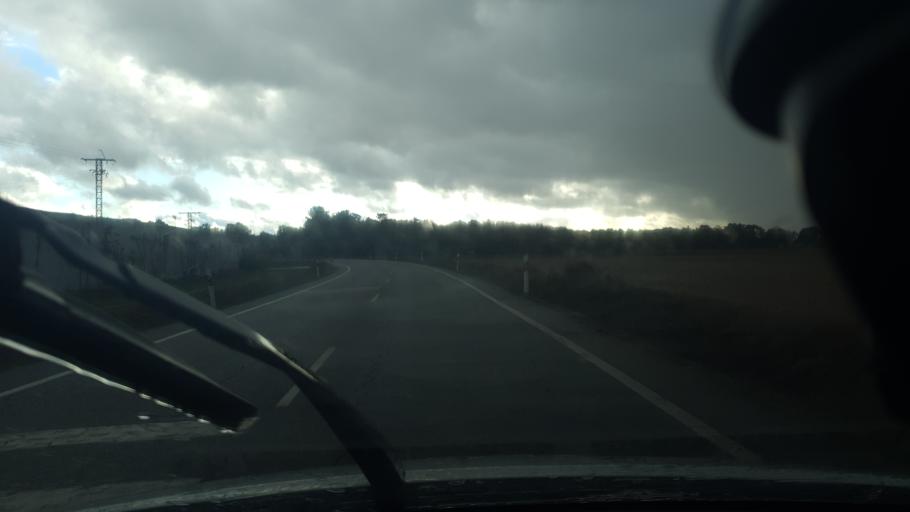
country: ES
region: Castille and Leon
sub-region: Provincia de Segovia
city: Samboal
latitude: 41.2968
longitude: -4.4093
